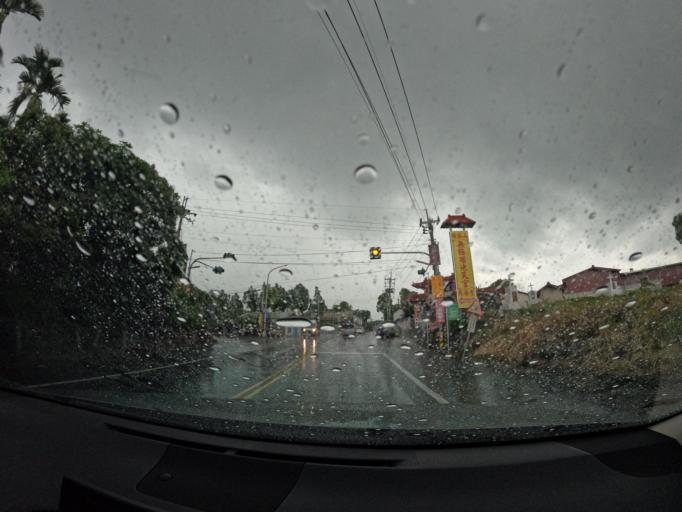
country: TW
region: Taiwan
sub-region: Nantou
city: Nantou
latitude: 23.9052
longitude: 120.6731
